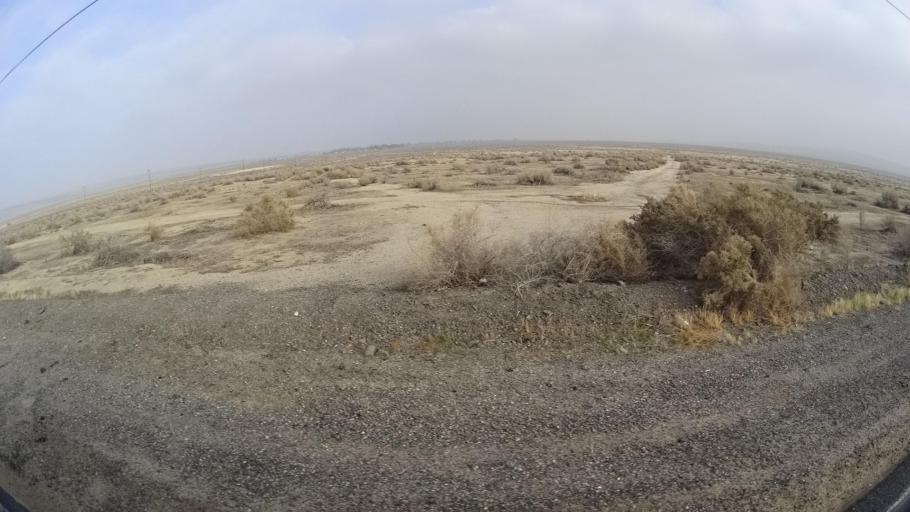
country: US
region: California
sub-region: Kern County
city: Ford City
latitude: 35.2085
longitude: -119.4457
